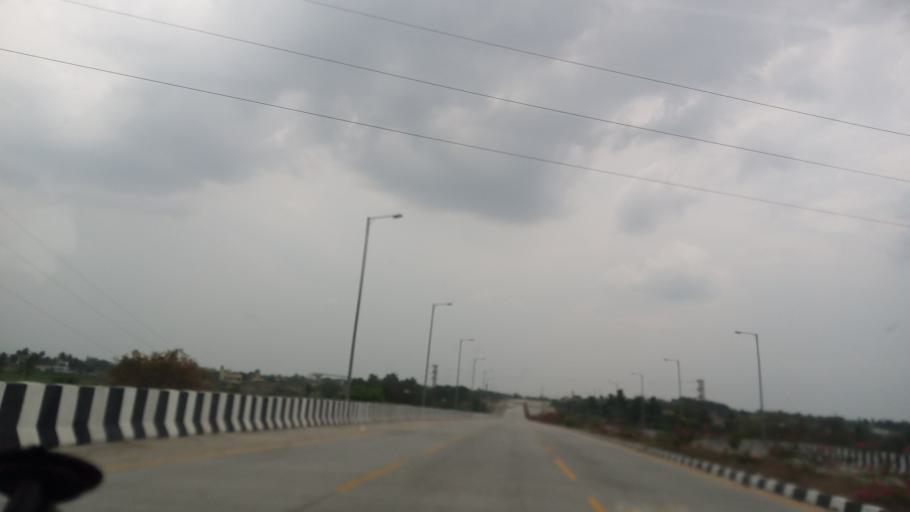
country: IN
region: Andhra Pradesh
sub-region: Chittoor
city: Palmaner
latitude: 13.2123
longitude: 78.7508
